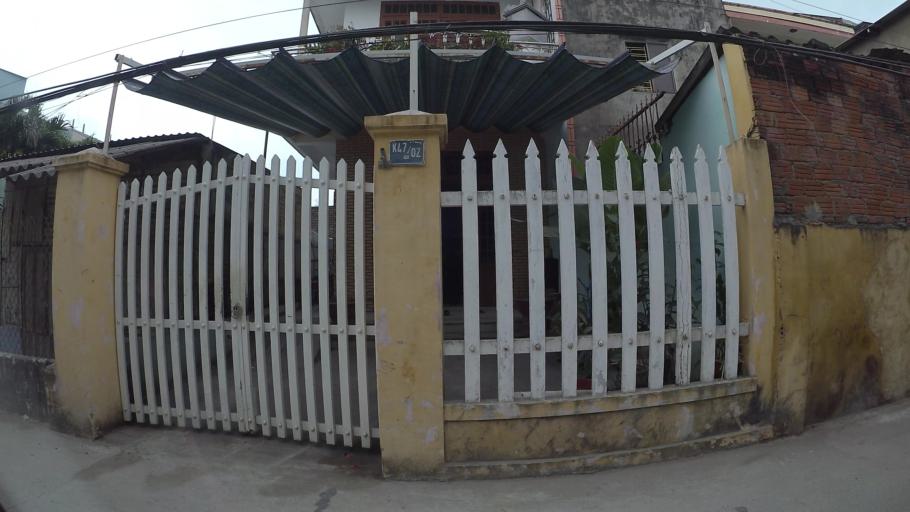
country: VN
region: Da Nang
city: Lien Chieu
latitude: 16.0550
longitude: 108.1632
